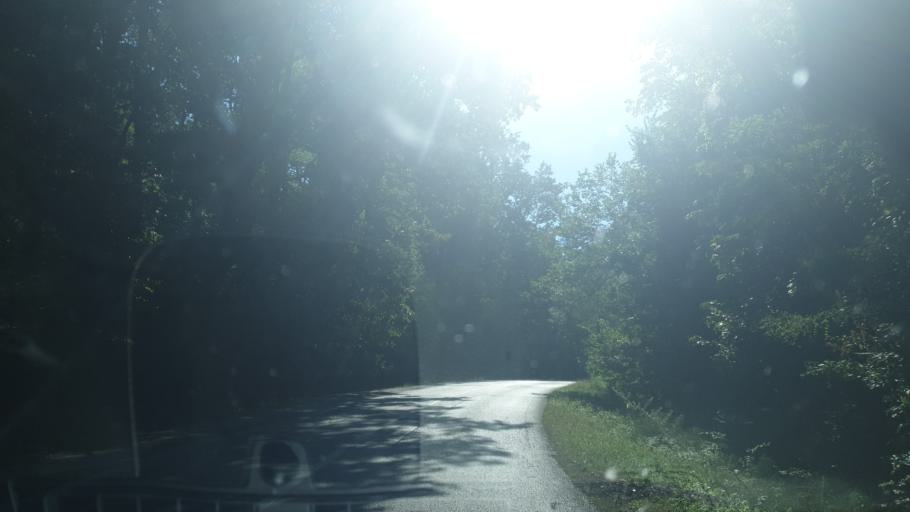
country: RS
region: Central Serbia
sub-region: Kolubarski Okrug
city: Lajkovac
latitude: 44.3147
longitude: 20.1835
